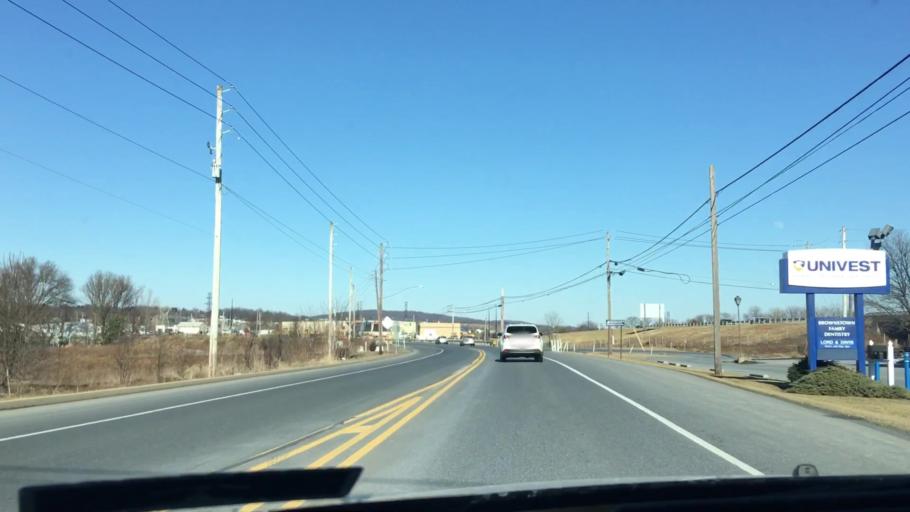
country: US
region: Pennsylvania
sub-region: Lancaster County
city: Brownstown
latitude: 40.1328
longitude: -76.2144
